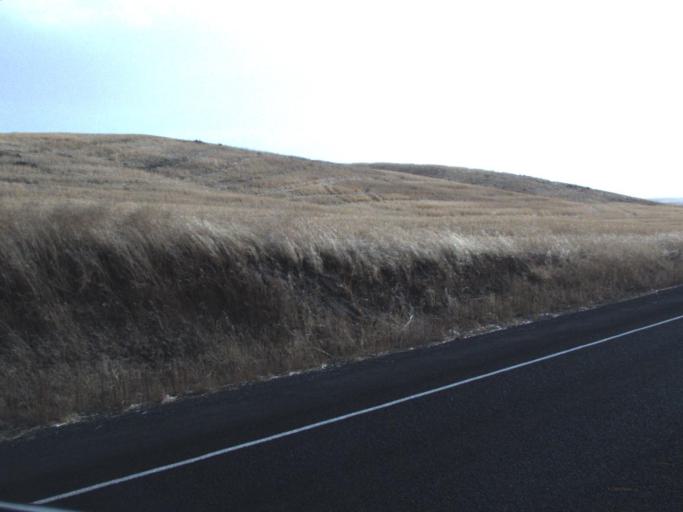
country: US
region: Washington
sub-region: Lincoln County
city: Davenport
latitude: 47.5171
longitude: -118.2155
